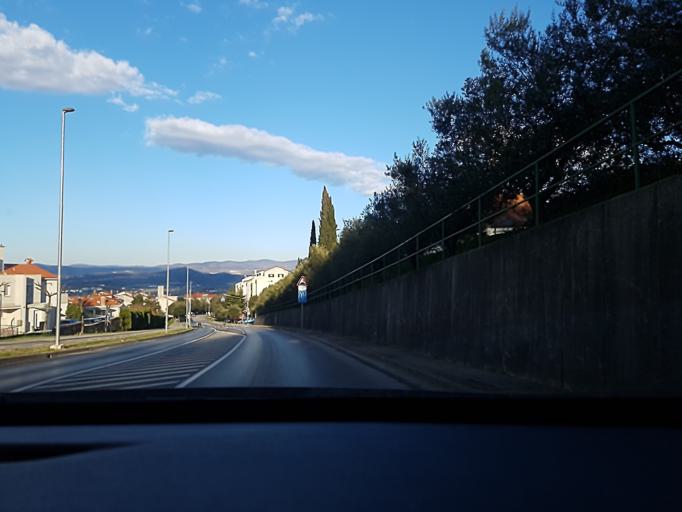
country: SI
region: Koper-Capodistria
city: Koper
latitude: 45.5390
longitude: 13.7048
